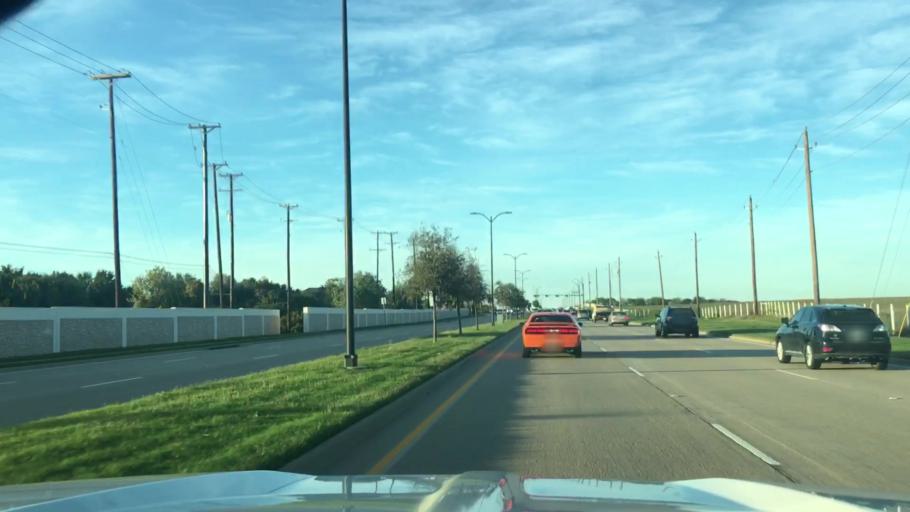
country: US
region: Texas
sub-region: Collin County
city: Frisco
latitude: 33.1606
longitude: -96.8032
